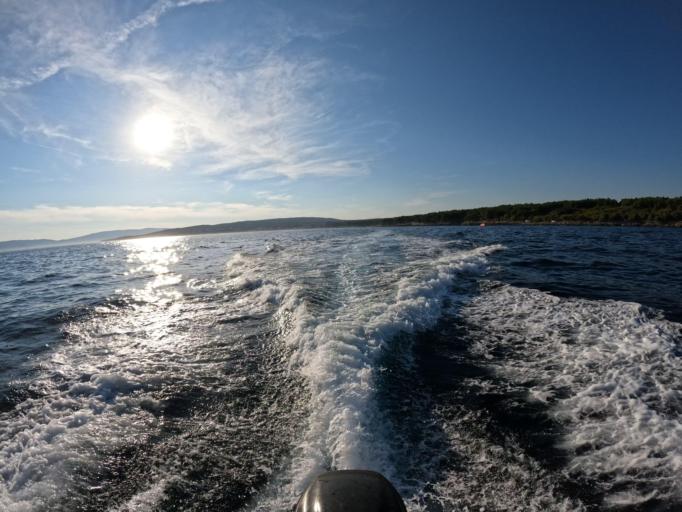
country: HR
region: Primorsko-Goranska
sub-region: Grad Krk
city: Krk
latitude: 45.0160
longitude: 14.5991
